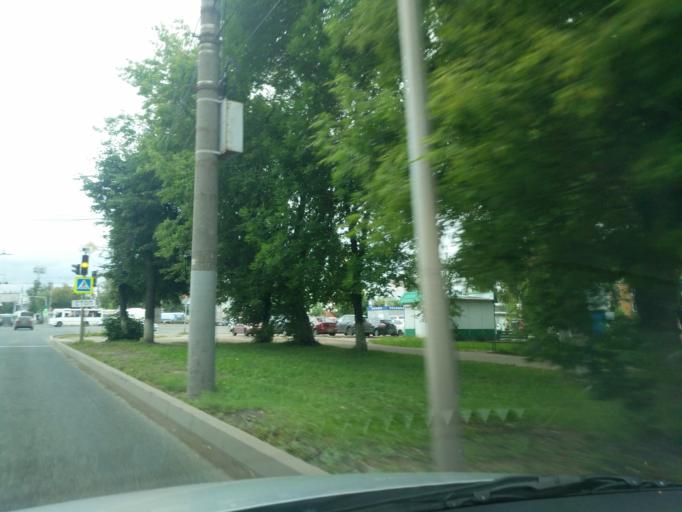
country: RU
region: Kirov
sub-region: Kirovo-Chepetskiy Rayon
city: Kirov
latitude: 58.6255
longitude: 49.6464
